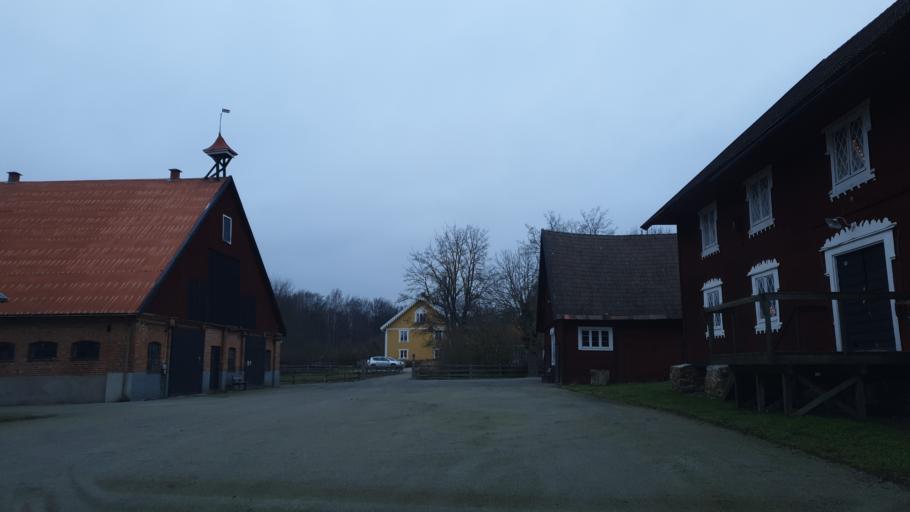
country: SE
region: Blekinge
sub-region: Karlskrona Kommun
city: Rodeby
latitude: 56.2186
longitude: 15.6767
